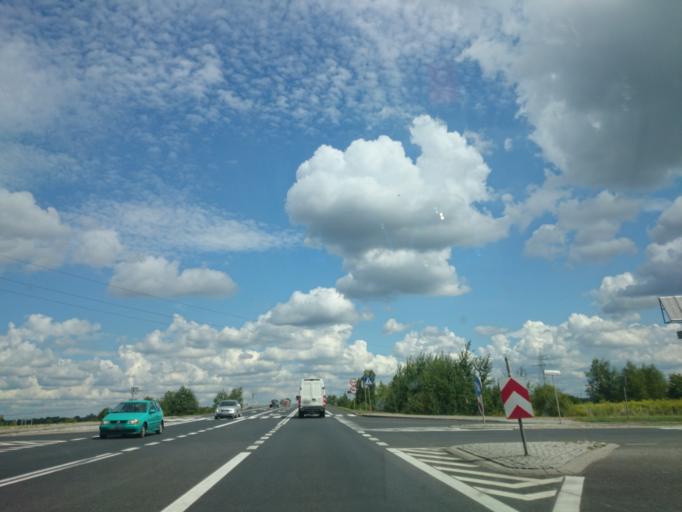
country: PL
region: Lower Silesian Voivodeship
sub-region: Legnica
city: Legnica
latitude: 51.2185
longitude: 16.1327
